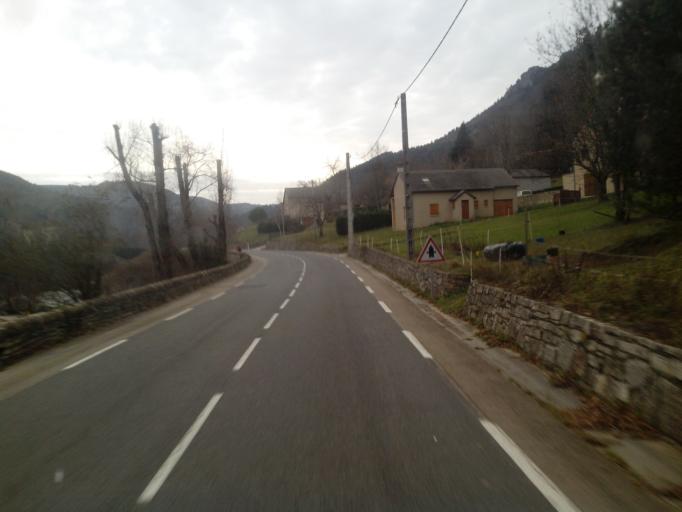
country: FR
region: Languedoc-Roussillon
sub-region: Departement de la Lozere
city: Florac
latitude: 44.3143
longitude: 3.5978
